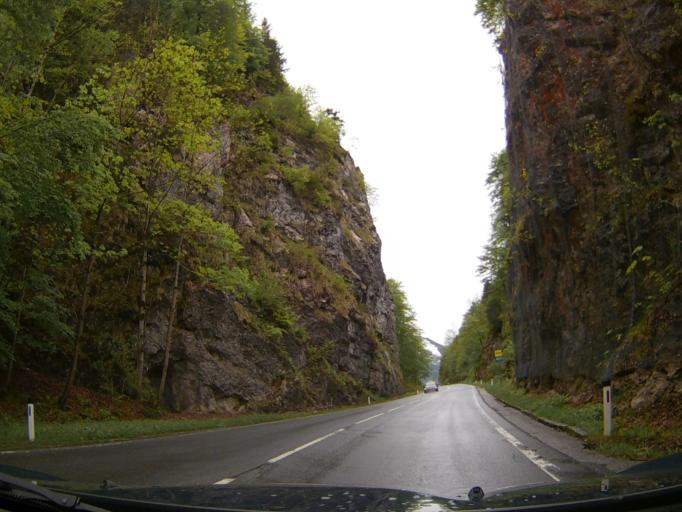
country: AT
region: Salzburg
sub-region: Politischer Bezirk Salzburg-Umgebung
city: Sankt Gilgen
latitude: 47.7883
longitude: 13.3921
